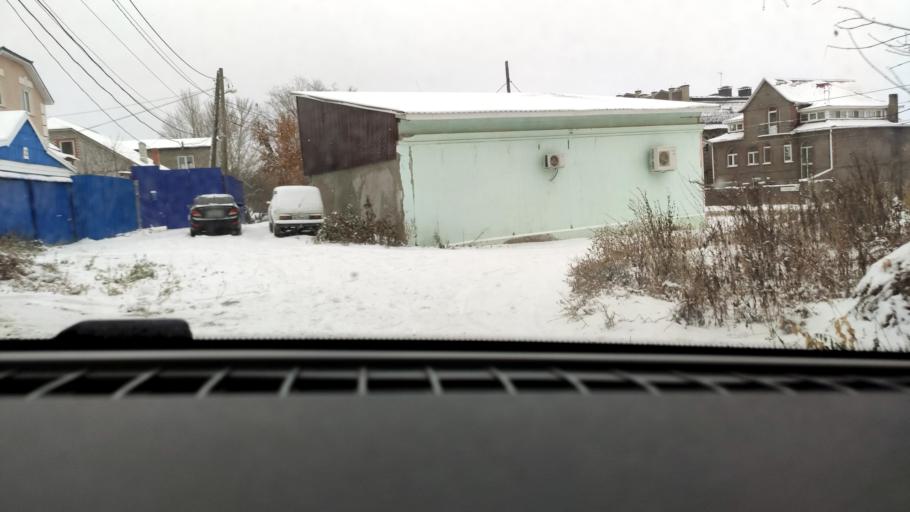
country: RU
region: Samara
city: Samara
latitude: 53.1819
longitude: 50.1561
